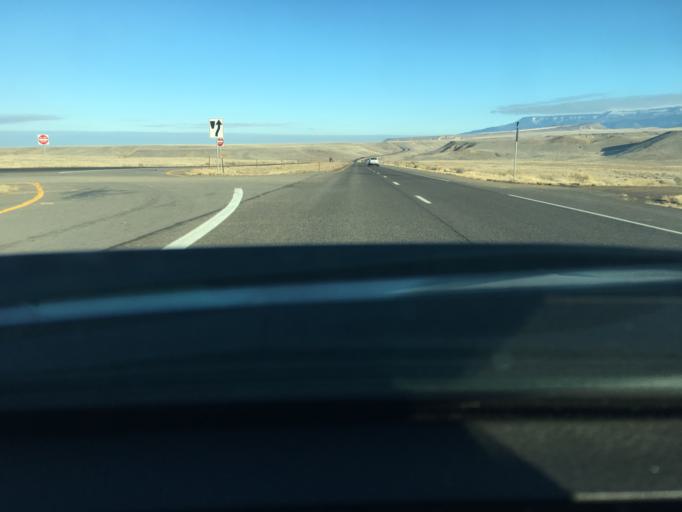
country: US
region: Colorado
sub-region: Delta County
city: Delta
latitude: 38.8158
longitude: -108.2959
